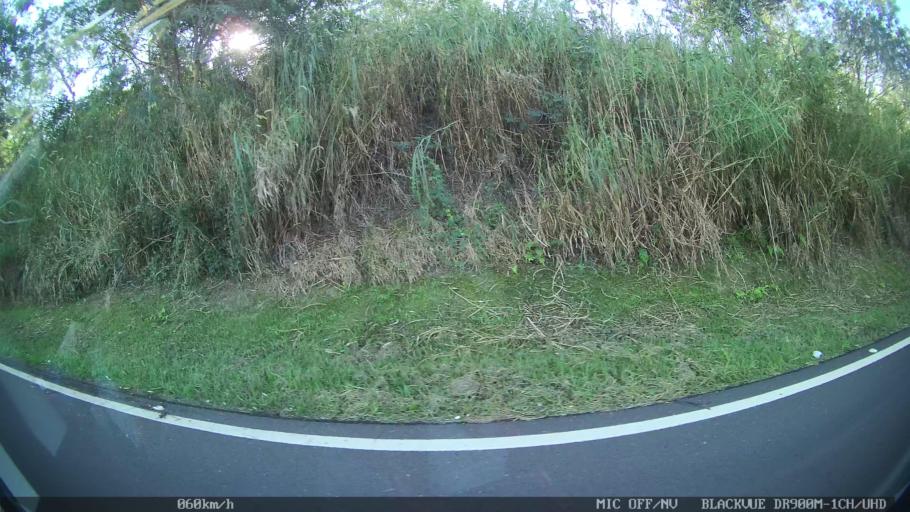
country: BR
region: Sao Paulo
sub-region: Piracicaba
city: Piracicaba
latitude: -22.6852
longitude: -47.5812
